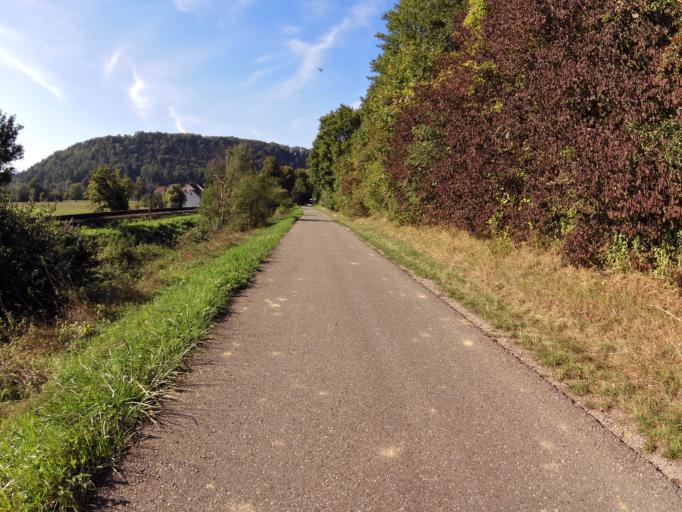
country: DE
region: Baden-Wuerttemberg
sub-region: Tuebingen Region
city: Rottenburg
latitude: 48.4633
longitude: 8.8992
